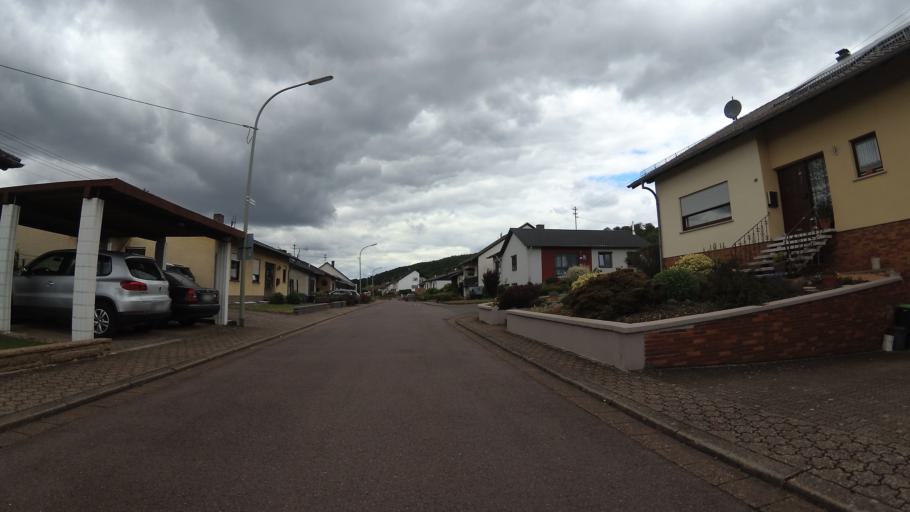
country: DE
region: Saarland
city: Schmelz
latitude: 49.3956
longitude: 6.8390
